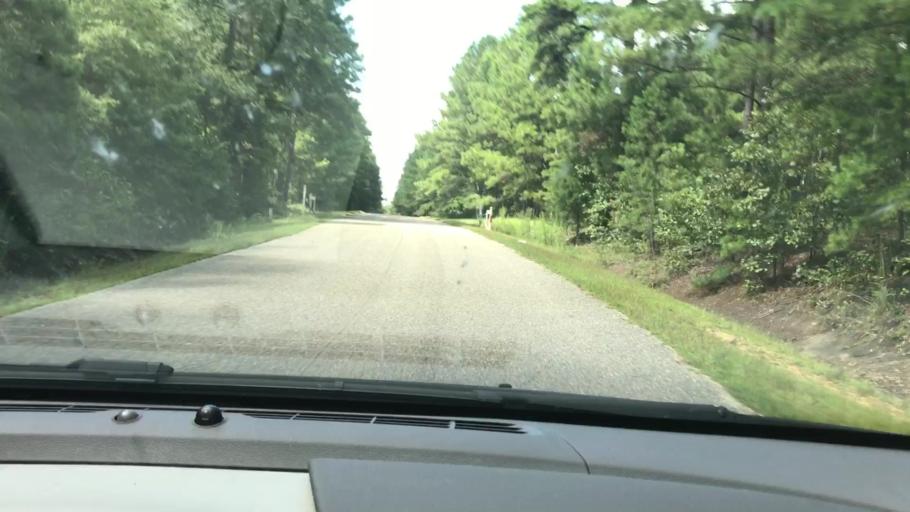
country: US
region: Georgia
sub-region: Clay County
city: Fort Gaines
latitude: 31.7414
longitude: -85.0757
